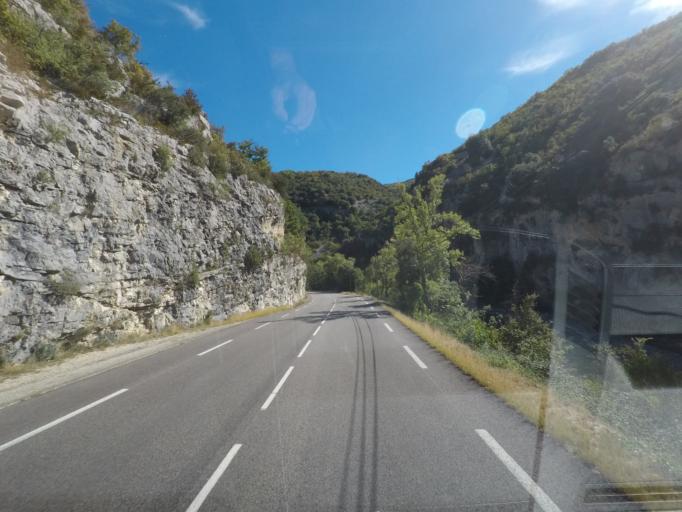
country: FR
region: Rhone-Alpes
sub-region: Departement de la Drome
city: Buis-les-Baronnies
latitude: 44.4325
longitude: 5.2846
